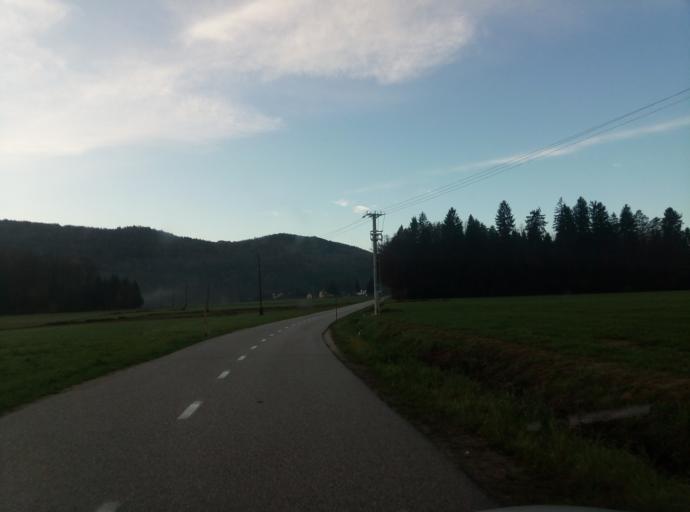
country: SI
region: Vodice
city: Vodice
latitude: 46.1676
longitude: 14.5191
